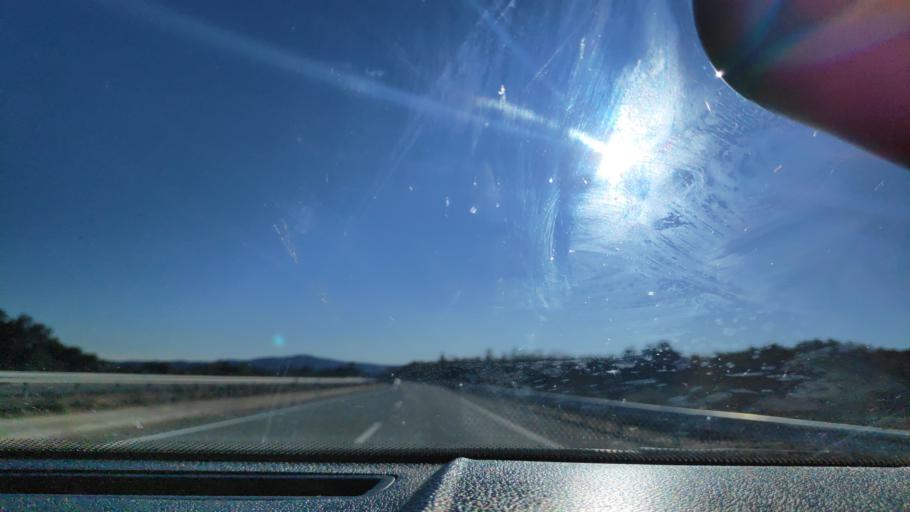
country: ES
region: Extremadura
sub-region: Provincia de Badajoz
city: Monesterio
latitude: 38.0114
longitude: -6.2289
